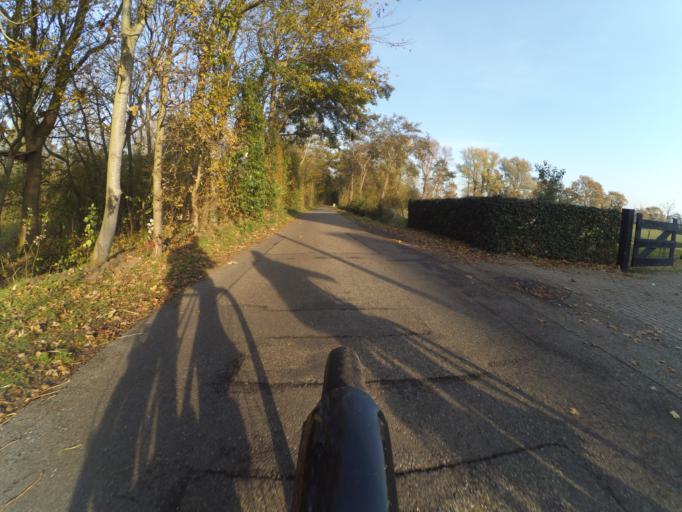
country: NL
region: South Holland
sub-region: Gemeente Goeree-Overflakkee
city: Goedereede
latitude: 51.8301
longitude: 3.9673
